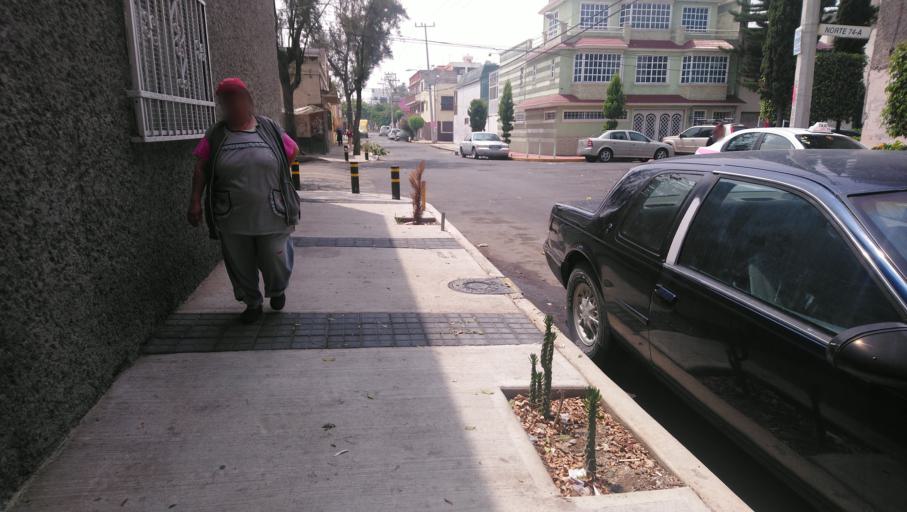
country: MX
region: Mexico City
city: Gustavo A. Madero
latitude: 19.4697
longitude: -99.1037
